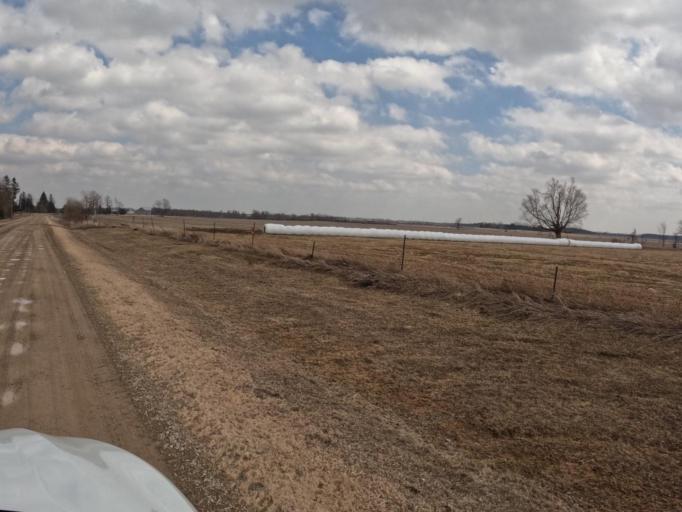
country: CA
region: Ontario
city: Shelburne
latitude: 44.0252
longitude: -80.2757
